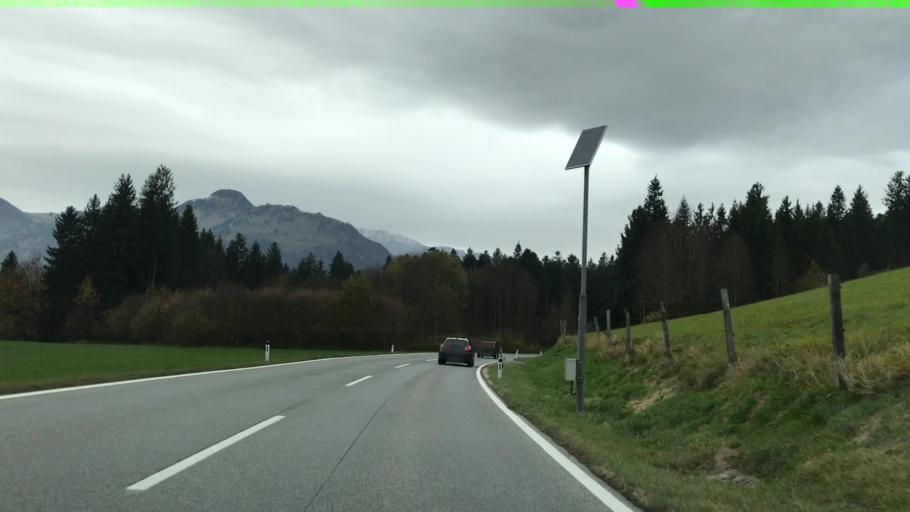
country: AT
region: Tyrol
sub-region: Politischer Bezirk Kitzbuhel
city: Kossen
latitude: 47.6573
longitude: 12.4267
